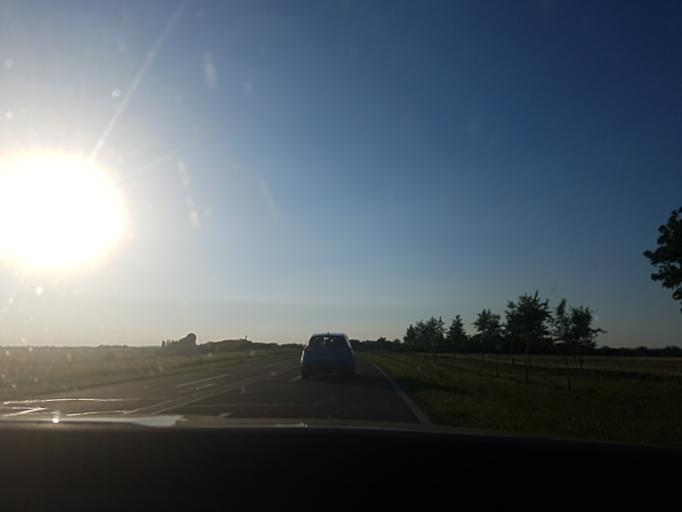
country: RO
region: Timis
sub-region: Comuna Moravita
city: Moravita
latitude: 45.2232
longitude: 21.2928
